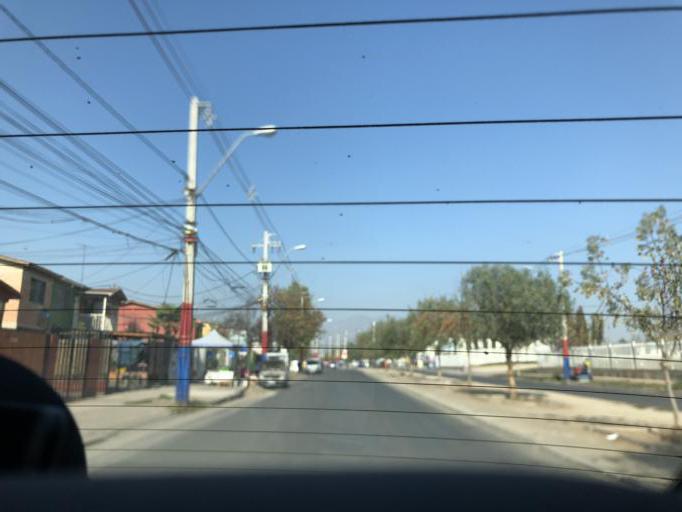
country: CL
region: Santiago Metropolitan
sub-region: Provincia de Cordillera
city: Puente Alto
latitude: -33.6242
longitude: -70.6125
